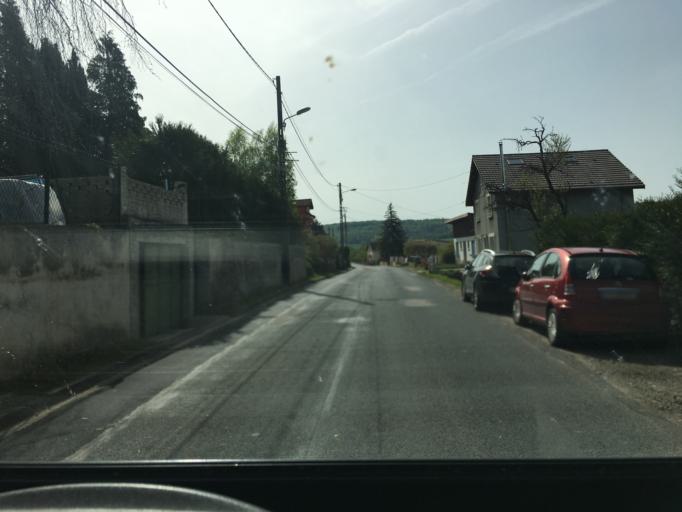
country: FR
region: Lorraine
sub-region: Departement de Meurthe-et-Moselle
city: Chaligny
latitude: 48.6322
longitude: 6.0485
